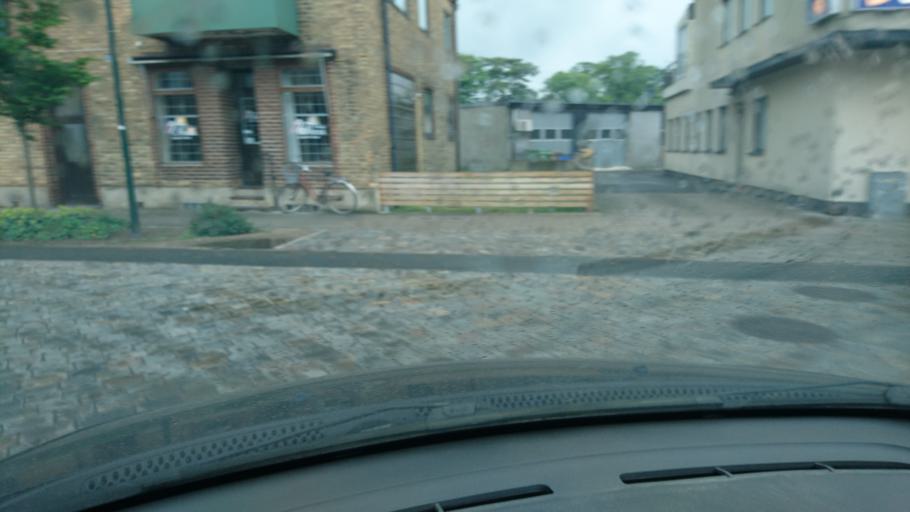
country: SE
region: Skane
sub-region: Tomelilla Kommun
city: Tomelilla
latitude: 55.5453
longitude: 13.9510
